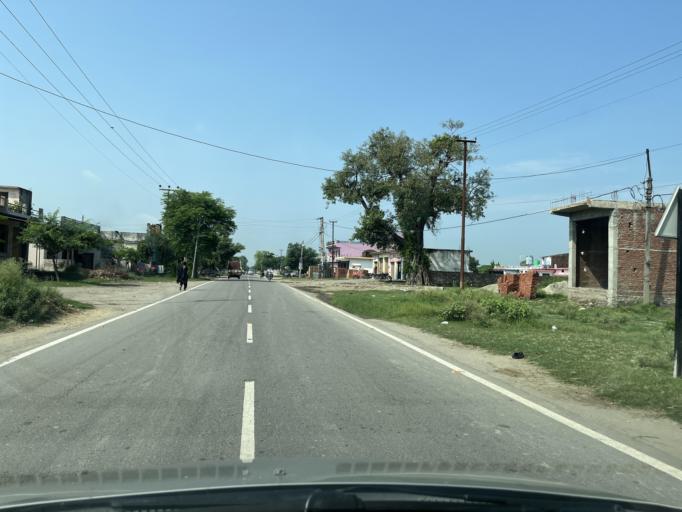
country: IN
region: Uttarakhand
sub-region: Udham Singh Nagar
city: Bazpur
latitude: 29.2097
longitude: 79.2149
